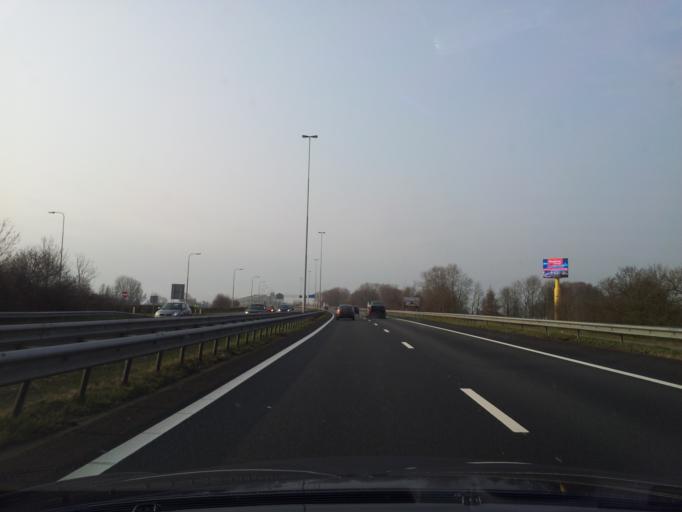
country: NL
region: North Brabant
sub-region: Gemeente Geertruidenberg
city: Geertruidenberg
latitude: 51.7266
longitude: 4.8944
